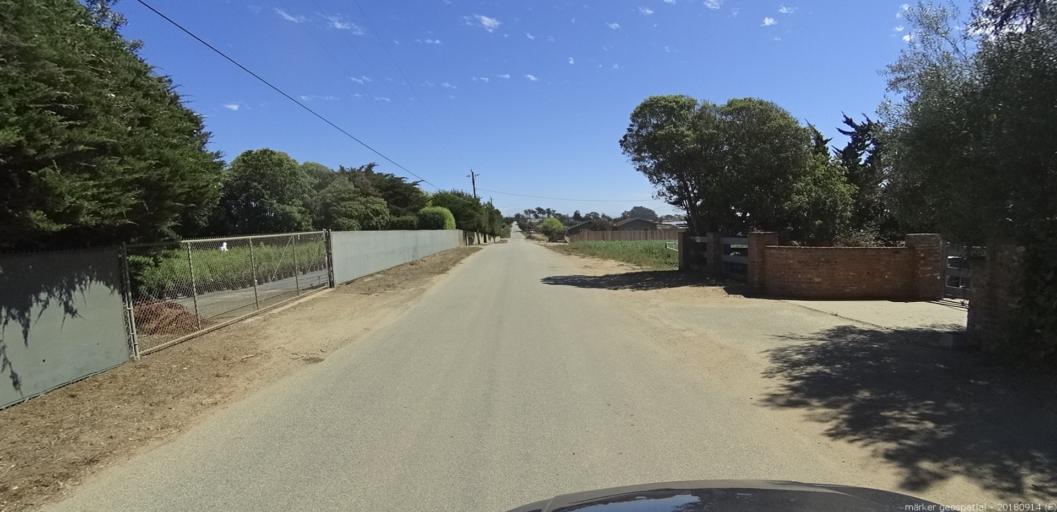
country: US
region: California
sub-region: Monterey County
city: Las Lomas
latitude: 36.8571
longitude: -121.7986
